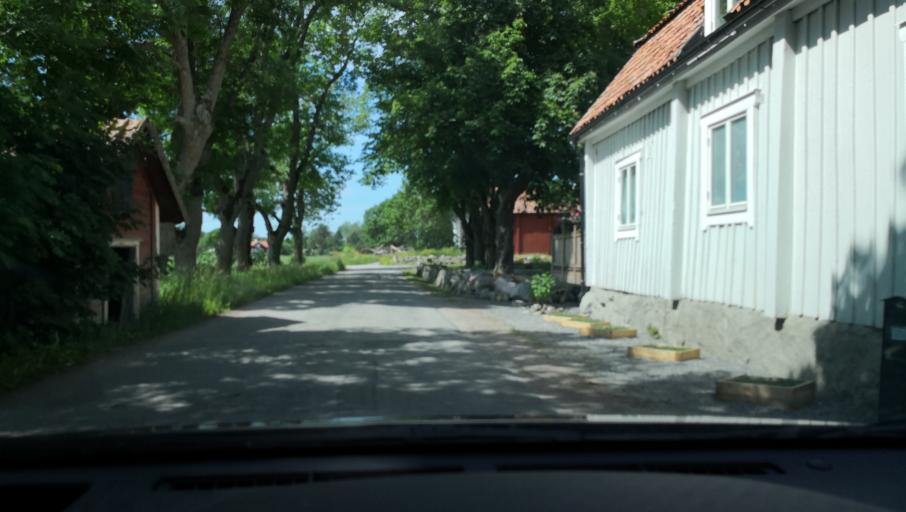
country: SE
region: Stockholm
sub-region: Sigtuna Kommun
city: Sigtuna
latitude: 59.6793
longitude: 17.6930
